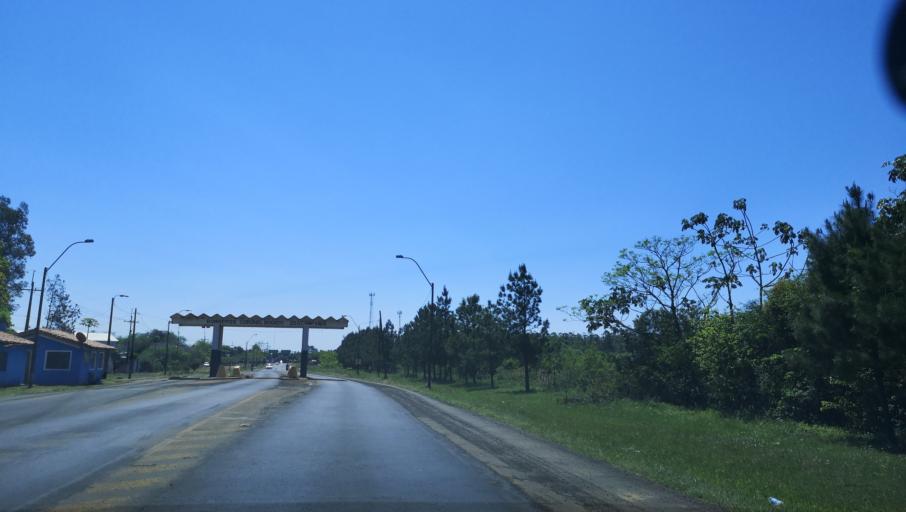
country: PY
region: Itapua
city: Carmen del Parana
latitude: -27.1765
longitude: -56.2252
